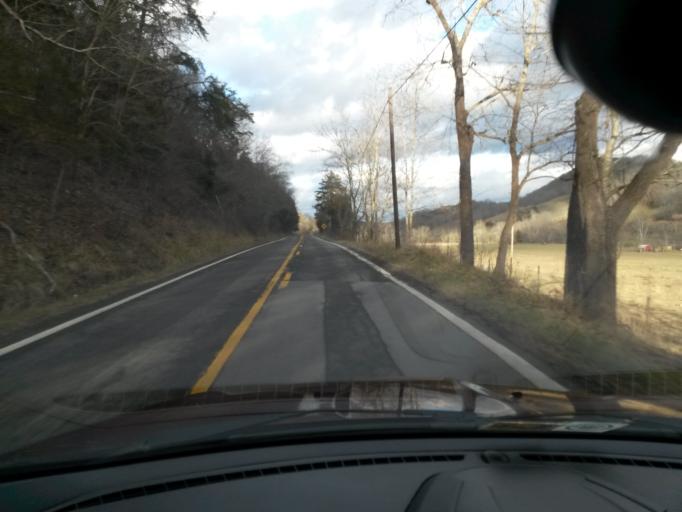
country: US
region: West Virginia
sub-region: Monroe County
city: Union
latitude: 37.5288
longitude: -80.6028
